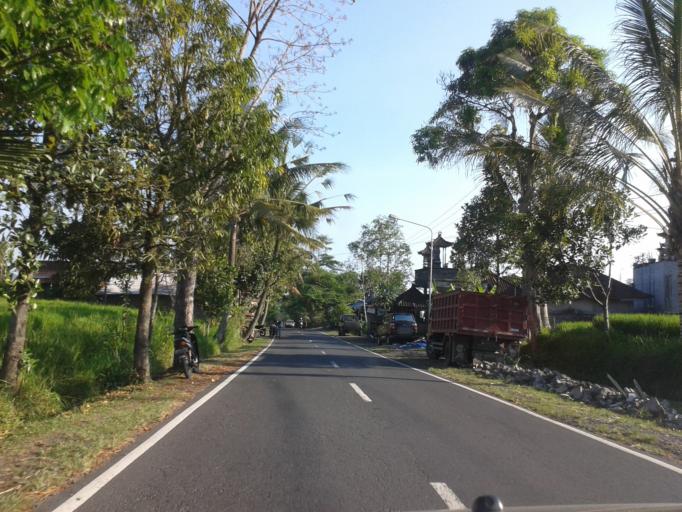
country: ID
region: Bali
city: Banjar Wangsian
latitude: -8.4871
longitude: 115.4014
